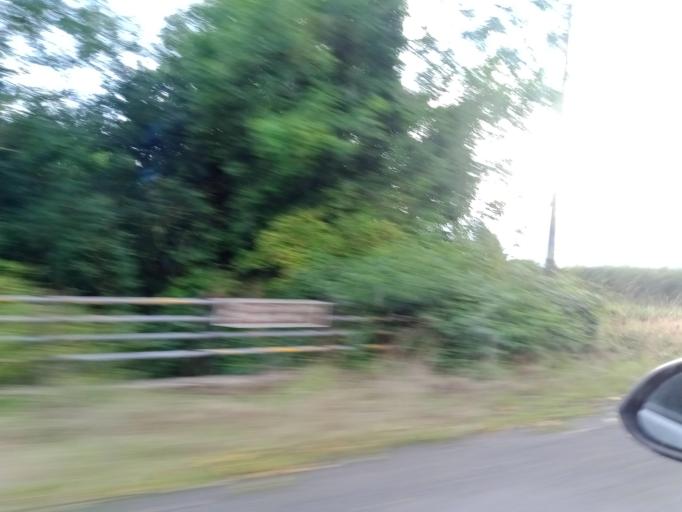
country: IE
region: Leinster
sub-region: Uibh Fhaili
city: Tullamore
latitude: 53.1464
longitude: -7.4840
